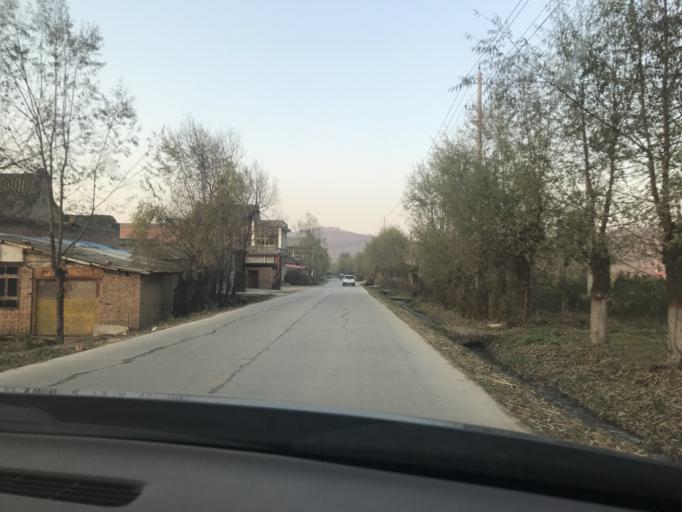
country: CN
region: Gansu Sheng
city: Maji
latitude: 35.4458
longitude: 103.0597
